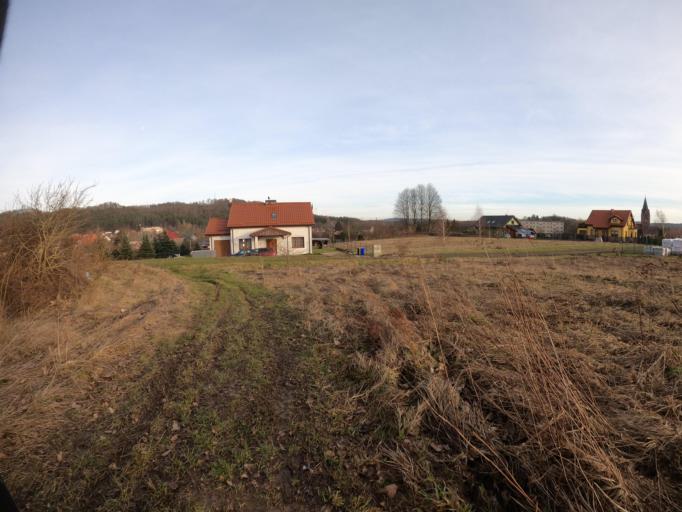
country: PL
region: West Pomeranian Voivodeship
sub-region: Powiat koszalinski
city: Polanow
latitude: 54.1215
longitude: 16.6830
